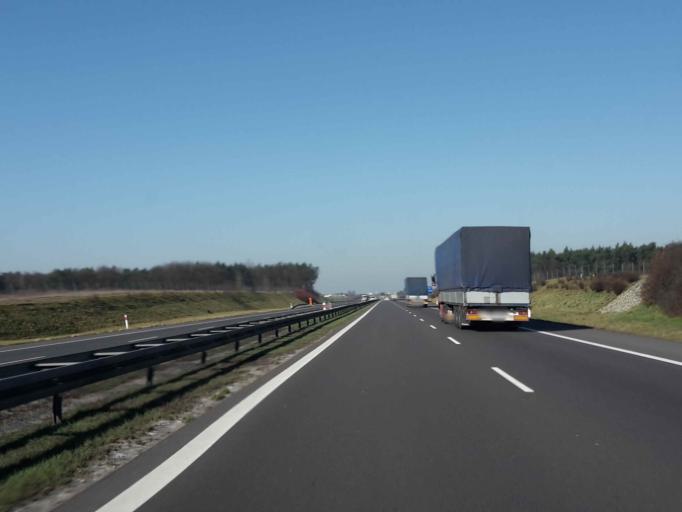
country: PL
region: Greater Poland Voivodeship
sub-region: Powiat poznanski
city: Swarzedz
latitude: 52.3362
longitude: 17.0578
